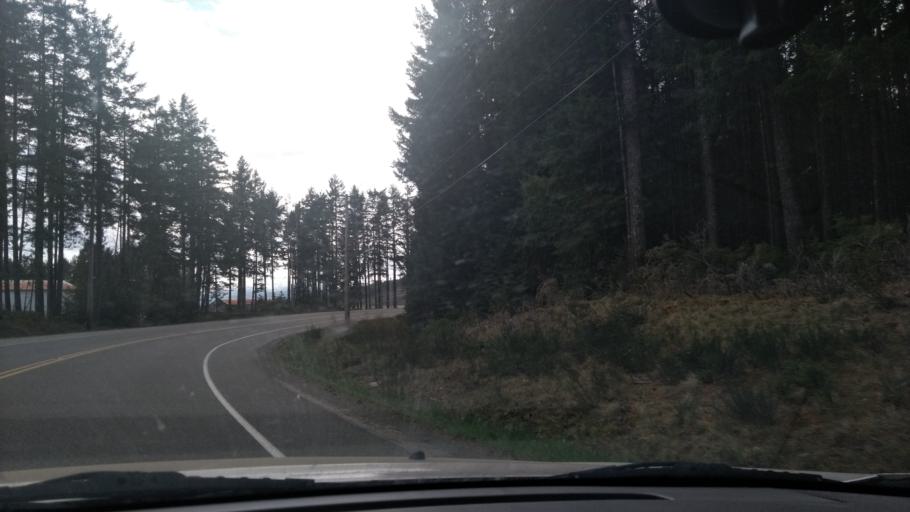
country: CA
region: British Columbia
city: Campbell River
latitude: 50.0089
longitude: -125.3565
